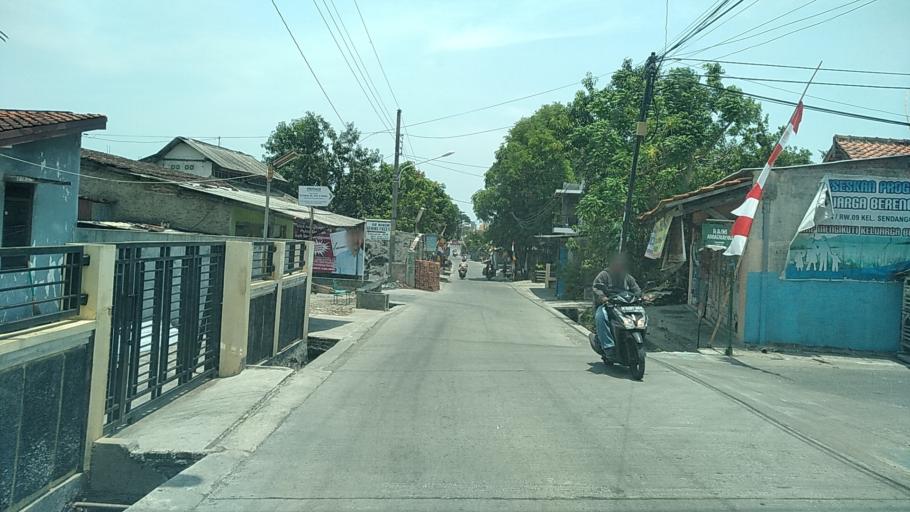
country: ID
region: Central Java
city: Semarang
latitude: -7.0110
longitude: 110.4549
